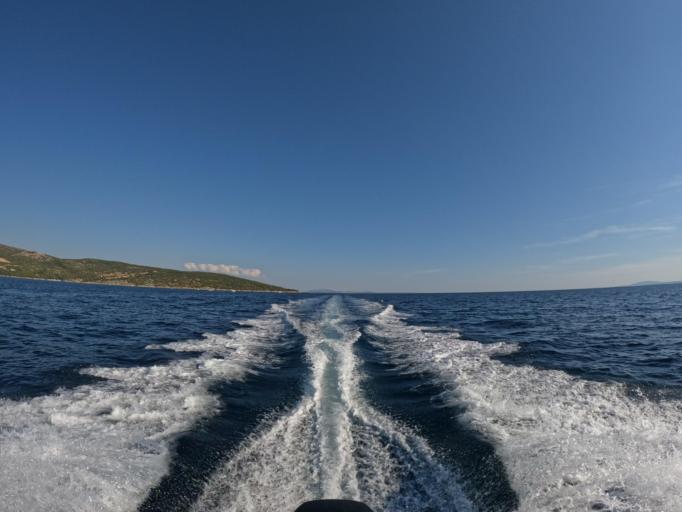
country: HR
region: Primorsko-Goranska
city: Punat
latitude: 44.9925
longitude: 14.6046
